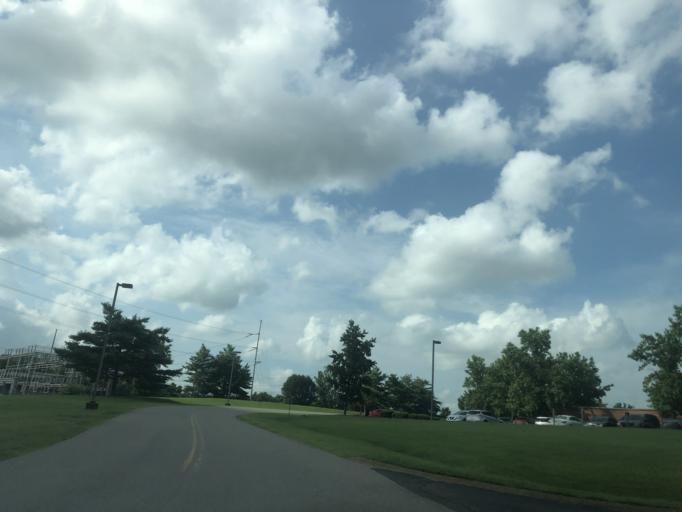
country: US
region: Tennessee
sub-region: Davidson County
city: Lakewood
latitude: 36.1634
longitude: -86.6484
